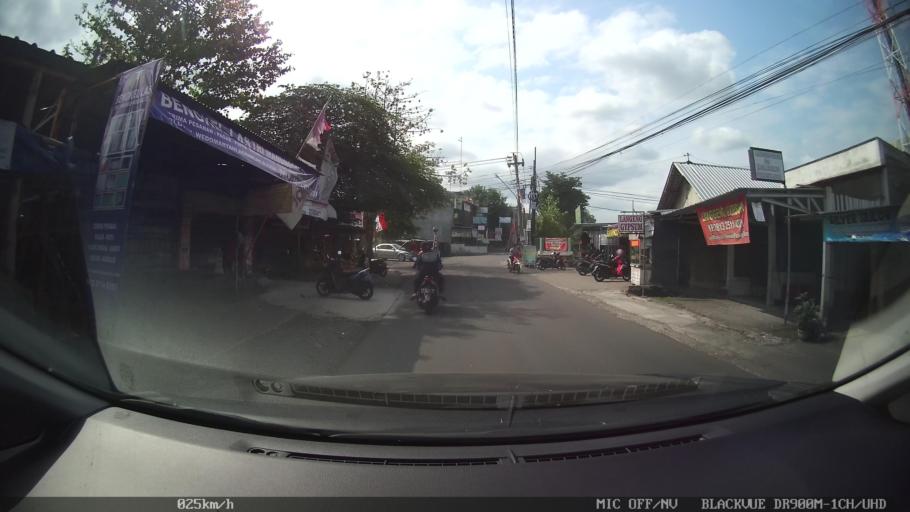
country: ID
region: Daerah Istimewa Yogyakarta
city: Depok
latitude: -7.7375
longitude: 110.4211
